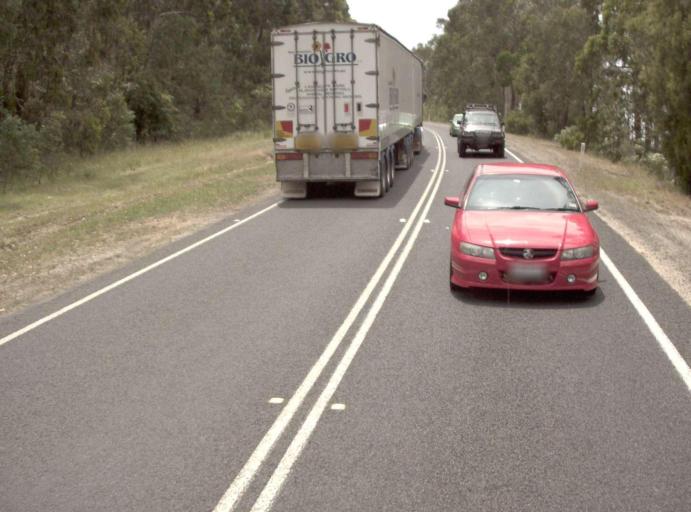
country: AU
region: Victoria
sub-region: Latrobe
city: Traralgon
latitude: -38.4571
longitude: 146.7360
